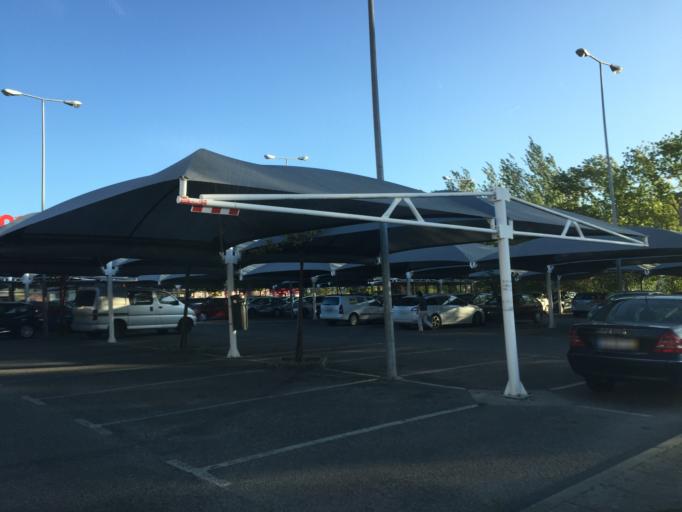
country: PT
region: Lisbon
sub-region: Torres Vedras
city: Torres Vedras
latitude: 39.0815
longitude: -9.2604
